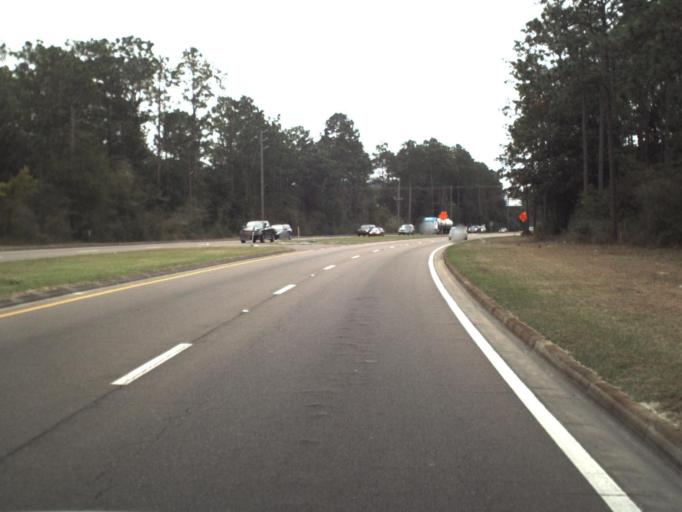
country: US
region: Florida
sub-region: Bay County
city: Springfield
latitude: 30.1709
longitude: -85.5915
